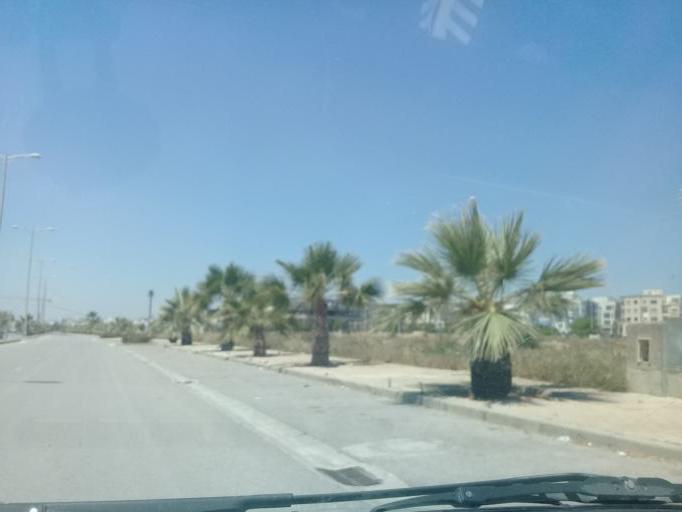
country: TN
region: Tunis
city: La Goulette
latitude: 36.8412
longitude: 10.2817
